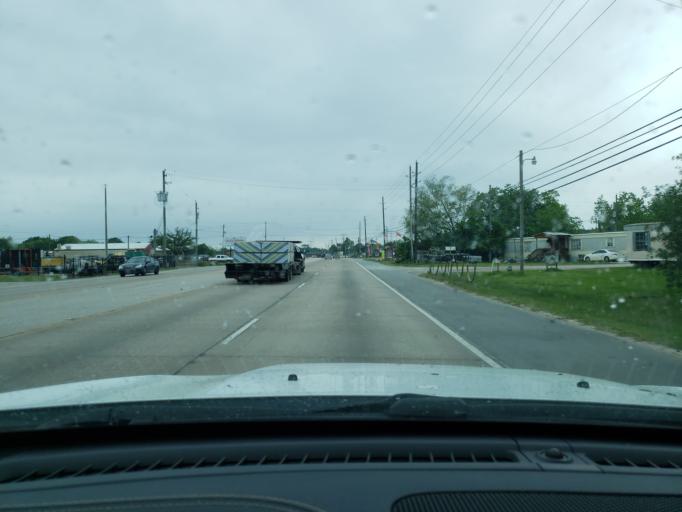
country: US
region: Texas
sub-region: Chambers County
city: Mont Belvieu
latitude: 29.8071
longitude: -94.9033
